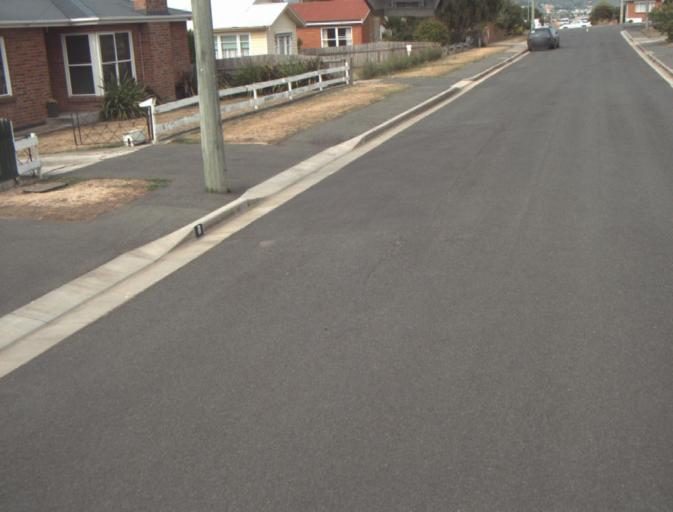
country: AU
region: Tasmania
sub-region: Launceston
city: Mayfield
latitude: -41.3791
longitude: 147.1287
